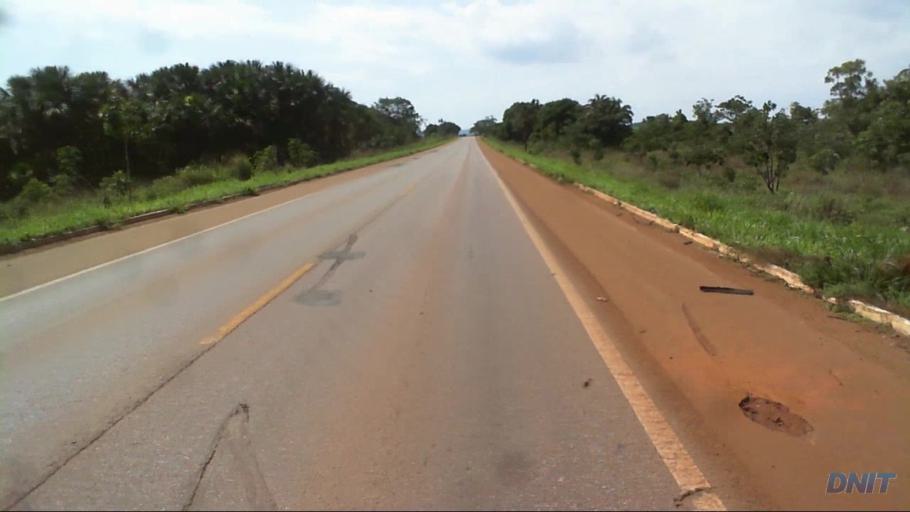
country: BR
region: Goias
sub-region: Barro Alto
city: Barro Alto
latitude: -15.0438
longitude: -48.8890
